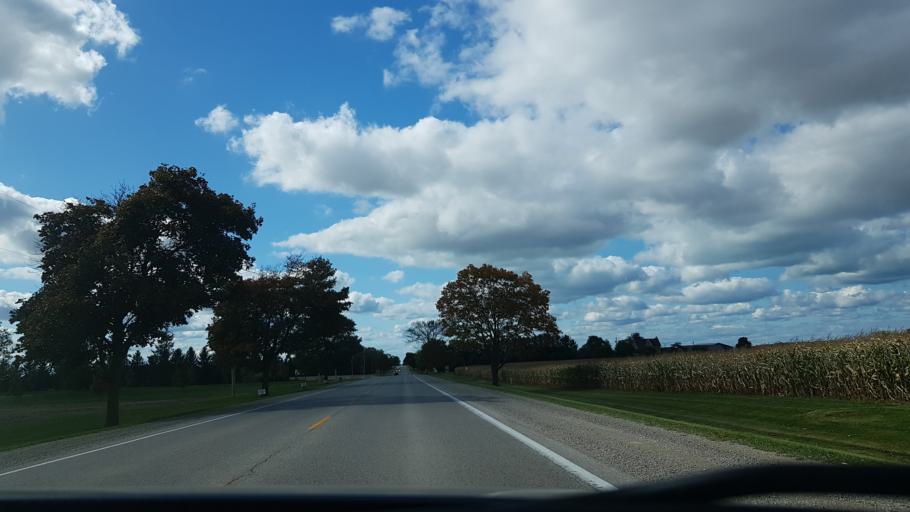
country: CA
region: Ontario
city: South Huron
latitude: 43.3480
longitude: -81.6163
